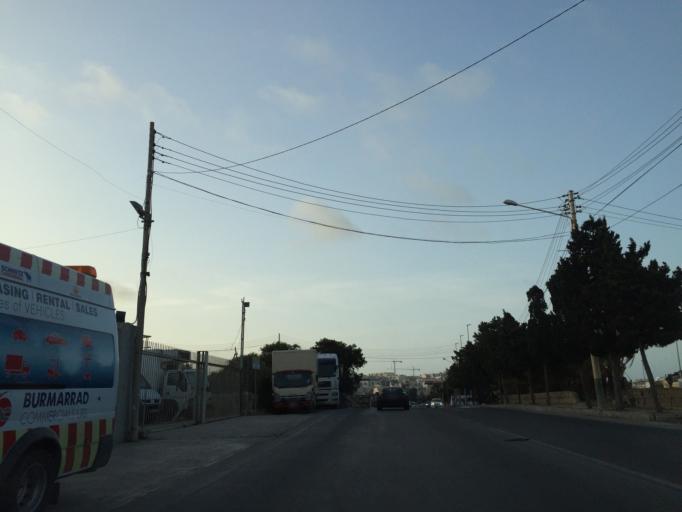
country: MT
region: Saint Paul's Bay
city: San Pawl il-Bahar
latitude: 35.9404
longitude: 14.4115
